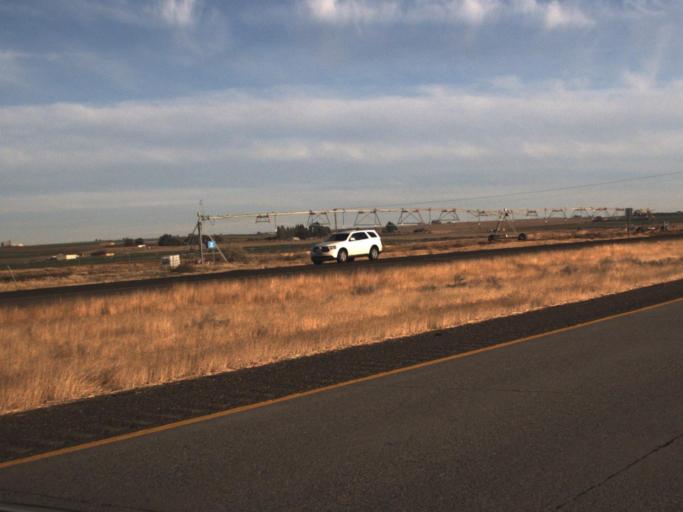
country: US
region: Washington
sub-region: Franklin County
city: Pasco
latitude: 46.3562
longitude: -119.0867
